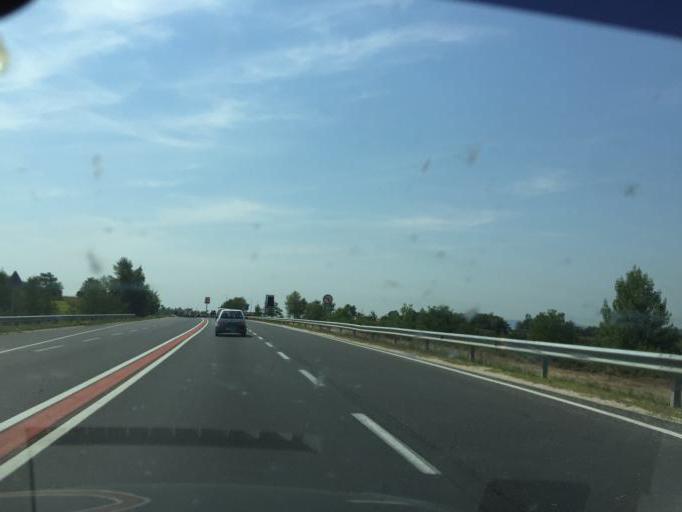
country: HU
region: Pest
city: Dunakeszi
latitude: 47.6599
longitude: 19.1610
